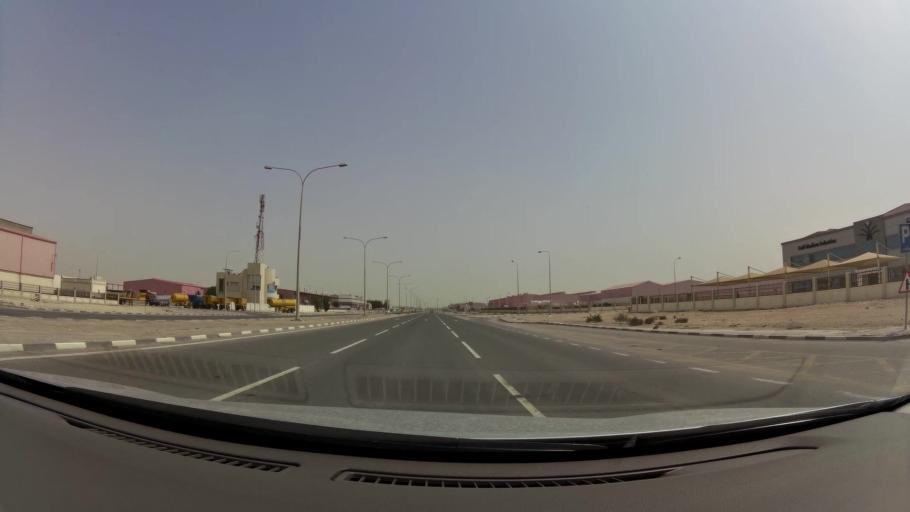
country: QA
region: Al Wakrah
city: Al Wukayr
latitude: 25.1551
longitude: 51.4014
